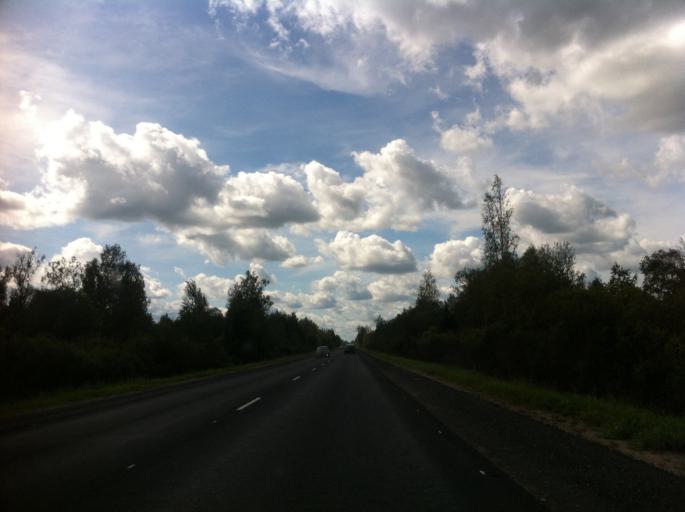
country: RU
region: Pskov
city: Izborsk
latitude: 57.7501
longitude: 28.0480
